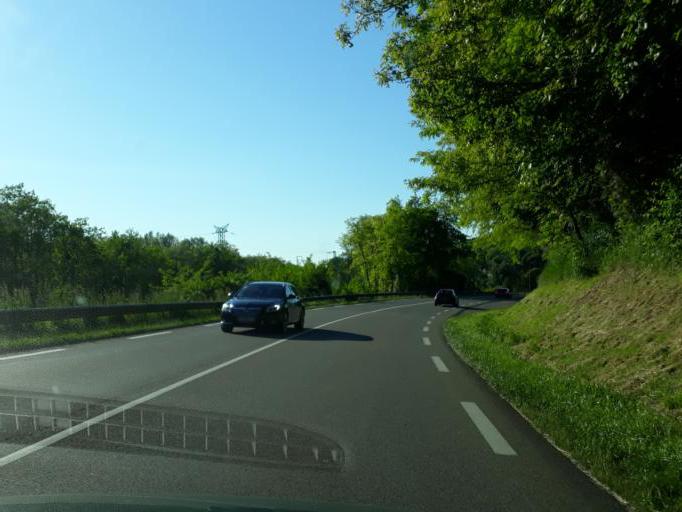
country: FR
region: Bourgogne
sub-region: Departement de la Nievre
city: Neuvy-sur-Loire
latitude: 47.5091
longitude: 2.8954
